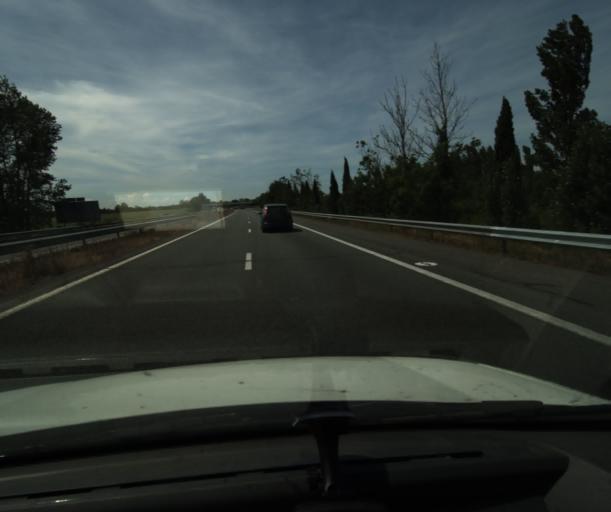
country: FR
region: Languedoc-Roussillon
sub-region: Departement de l'Aude
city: Bram
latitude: 43.2335
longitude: 2.1053
